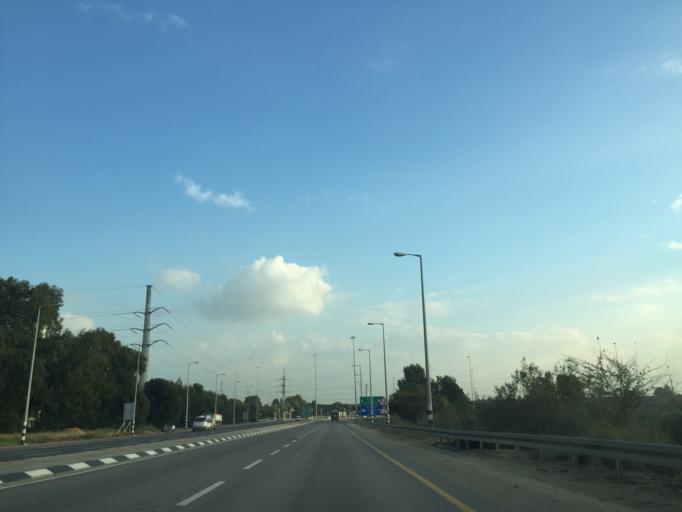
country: IL
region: Central District
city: Ramla
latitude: 31.9151
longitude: 34.8884
